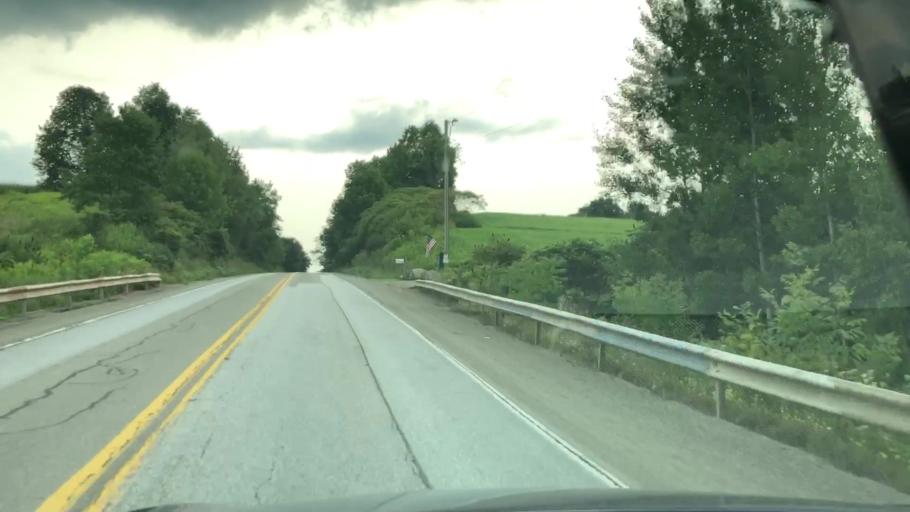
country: US
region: Pennsylvania
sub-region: Erie County
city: Union City
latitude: 41.9916
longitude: -79.8178
